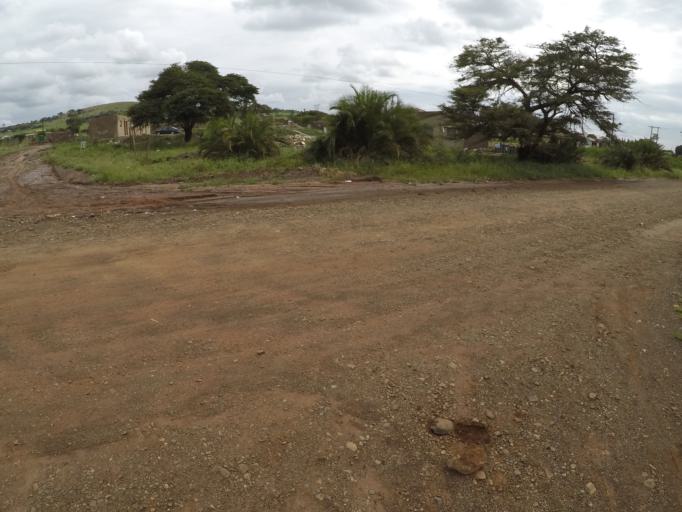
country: ZA
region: KwaZulu-Natal
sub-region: uThungulu District Municipality
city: Empangeni
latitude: -28.7129
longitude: 31.8611
